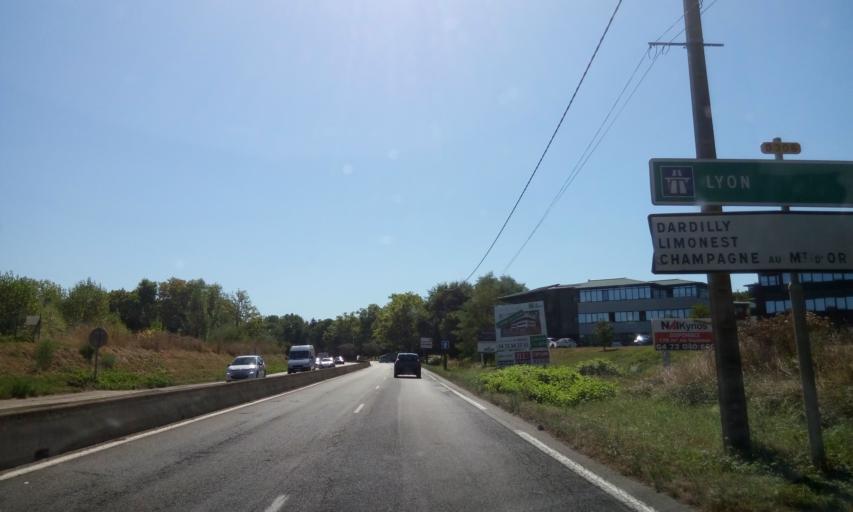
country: FR
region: Rhone-Alpes
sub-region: Departement du Rhone
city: Lissieu
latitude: 45.8425
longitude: 4.7354
